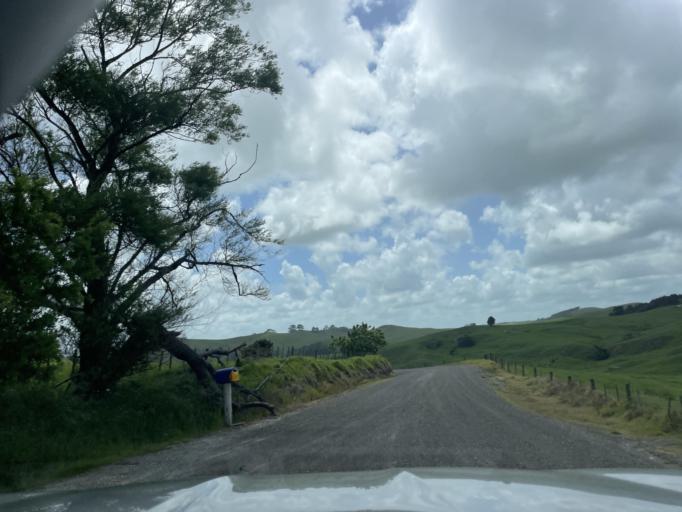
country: NZ
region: Auckland
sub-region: Auckland
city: Wellsford
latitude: -36.1981
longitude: 174.3365
